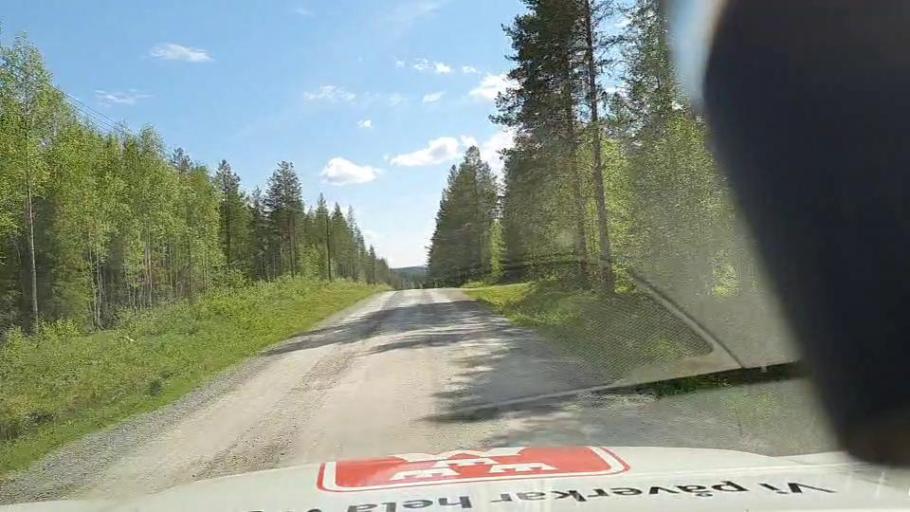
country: SE
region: Jaemtland
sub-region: Stroemsunds Kommun
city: Stroemsund
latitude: 64.4750
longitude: 15.5934
